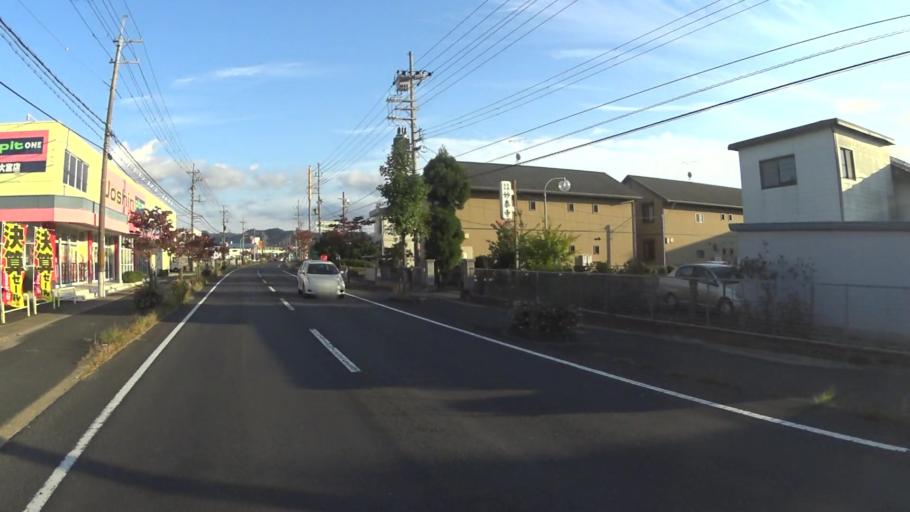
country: JP
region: Kyoto
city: Miyazu
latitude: 35.5949
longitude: 135.0910
